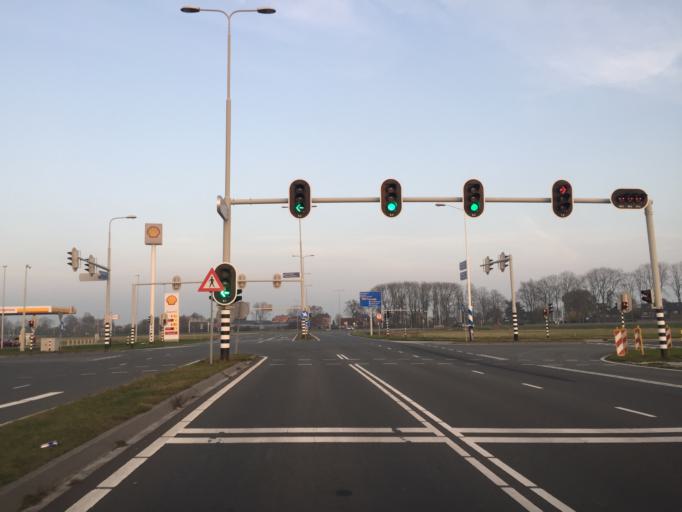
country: NL
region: South Holland
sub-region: Gemeente Lansingerland
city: Bleiswijk
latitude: 52.0406
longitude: 4.5391
